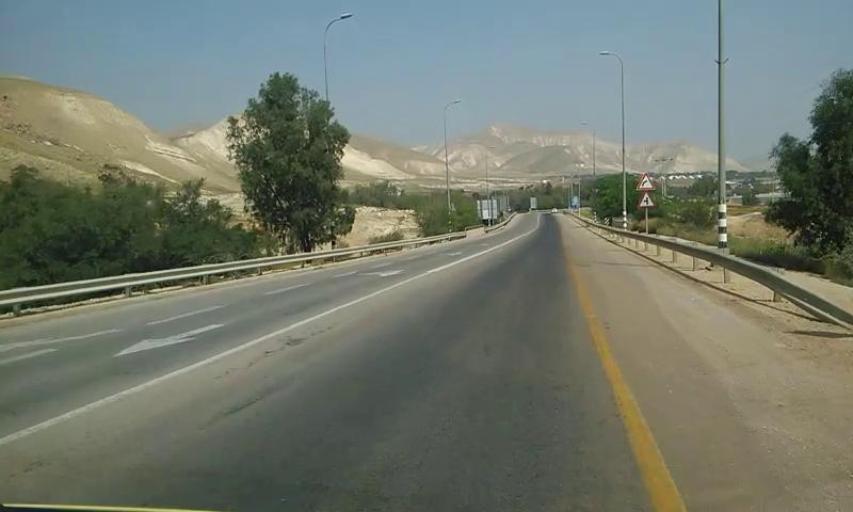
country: PS
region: West Bank
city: Al Fasayil
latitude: 32.0499
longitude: 35.4644
